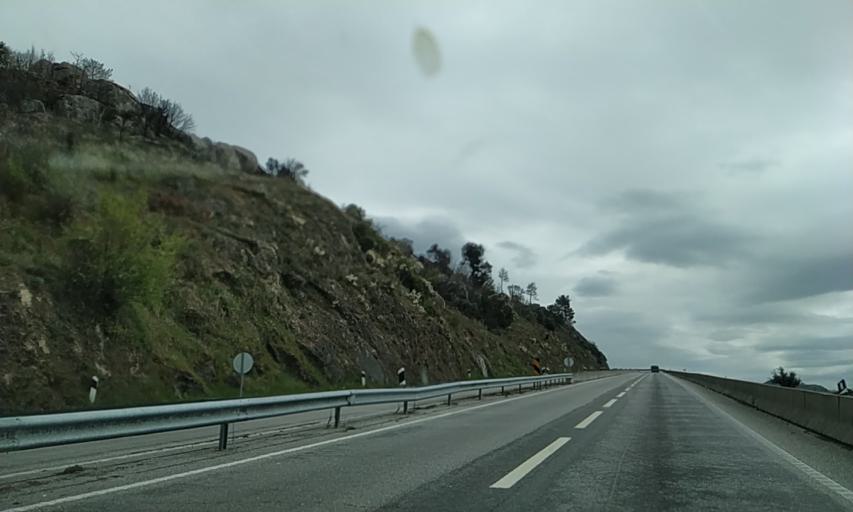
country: PT
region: Guarda
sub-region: Guarda
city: Guarda
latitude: 40.5995
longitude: -7.2753
